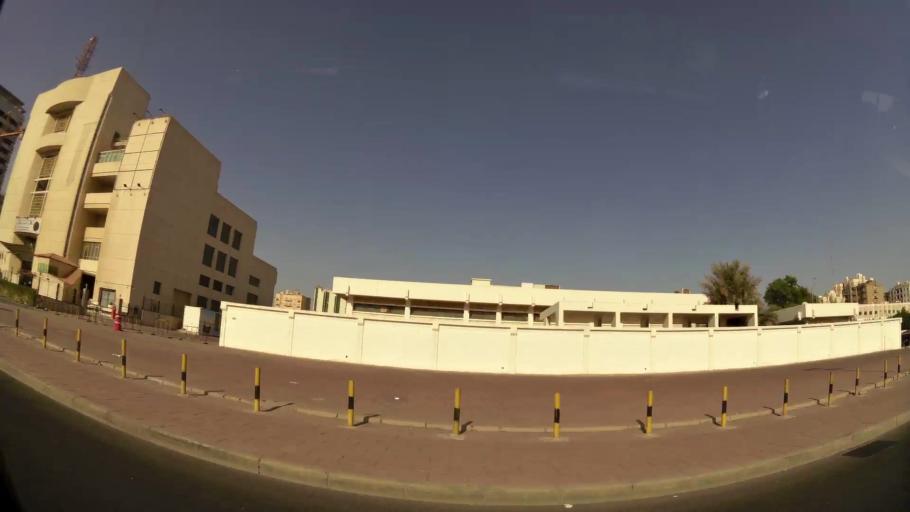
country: KW
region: Muhafazat Hawalli
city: As Salimiyah
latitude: 29.3292
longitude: 48.0824
